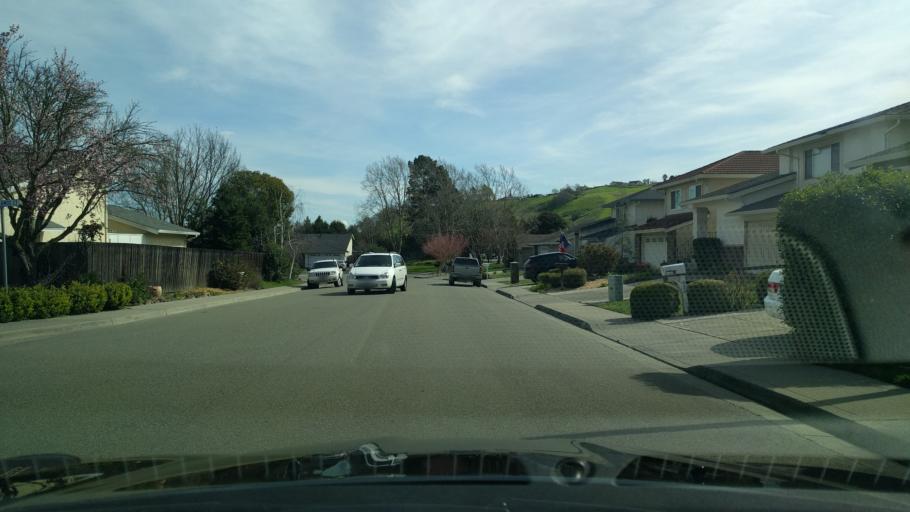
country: US
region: California
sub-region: Contra Costa County
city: San Ramon
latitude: 37.7625
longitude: -121.9733
